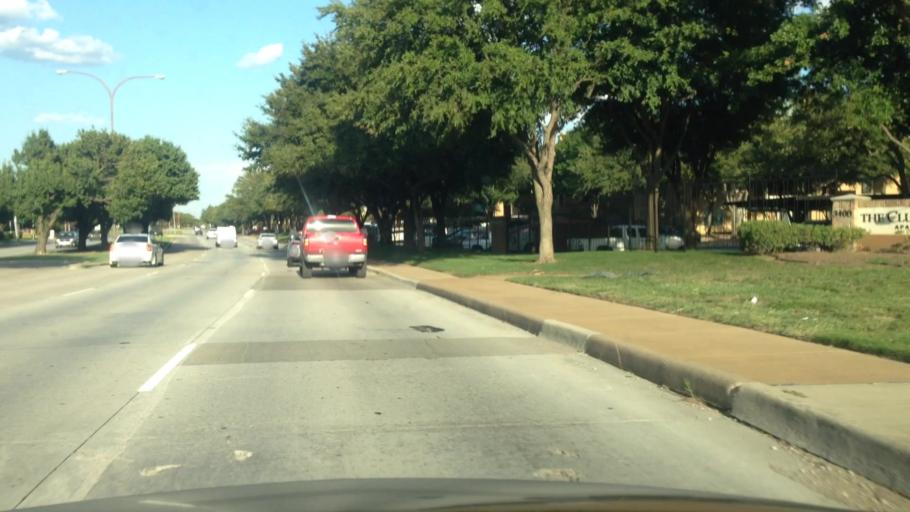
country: US
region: Texas
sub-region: Tarrant County
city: Blue Mound
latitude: 32.8607
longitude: -97.3117
